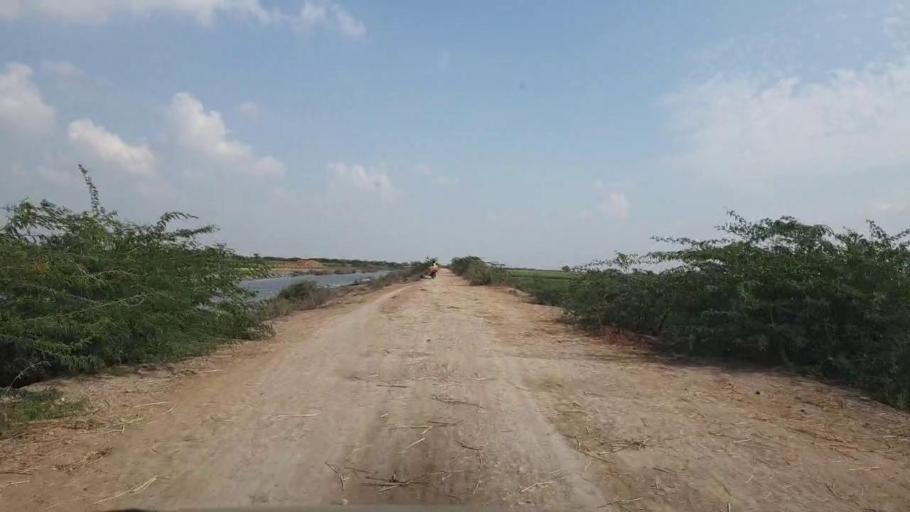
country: PK
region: Sindh
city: Badin
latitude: 24.4737
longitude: 68.5919
